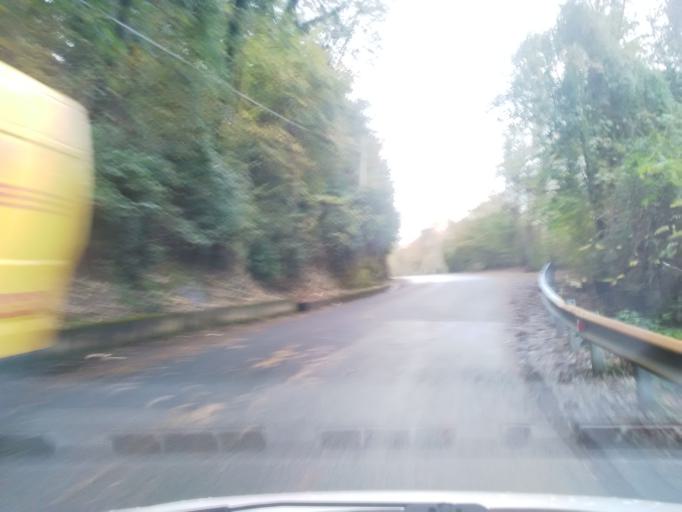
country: IT
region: Piedmont
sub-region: Provincia Verbano-Cusio-Ossola
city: Madonna del Sasso
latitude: 45.7999
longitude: 8.3743
